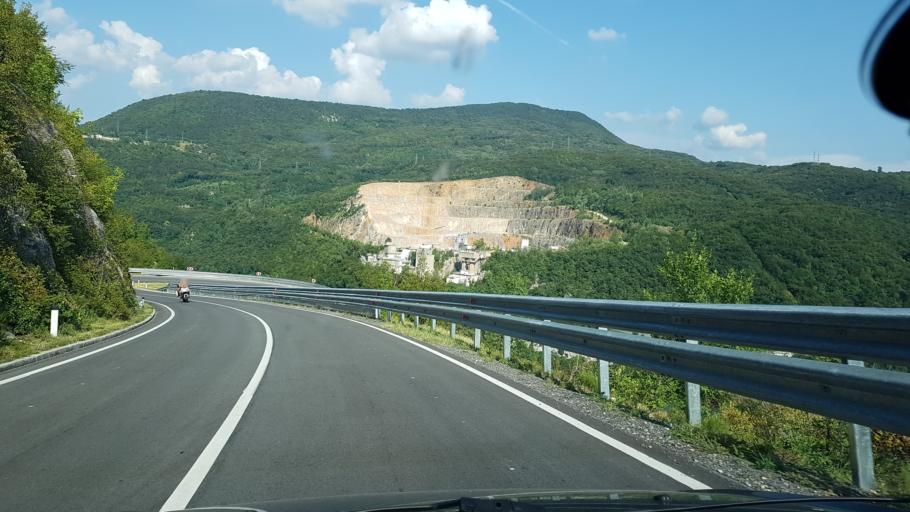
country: SI
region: Nova Gorica
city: Solkan
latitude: 45.9769
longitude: 13.6442
